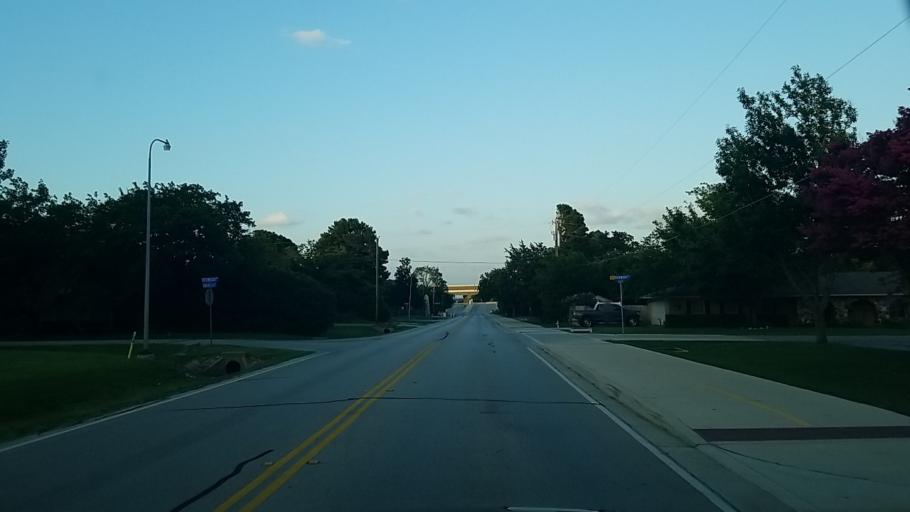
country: US
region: Texas
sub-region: Denton County
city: Highland Village
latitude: 33.0901
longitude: -97.0331
